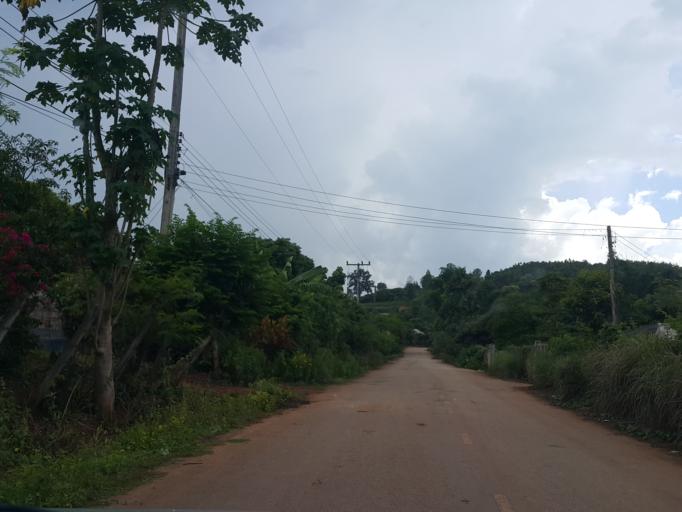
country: TH
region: Chiang Mai
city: Phrao
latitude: 19.3309
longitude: 99.1490
